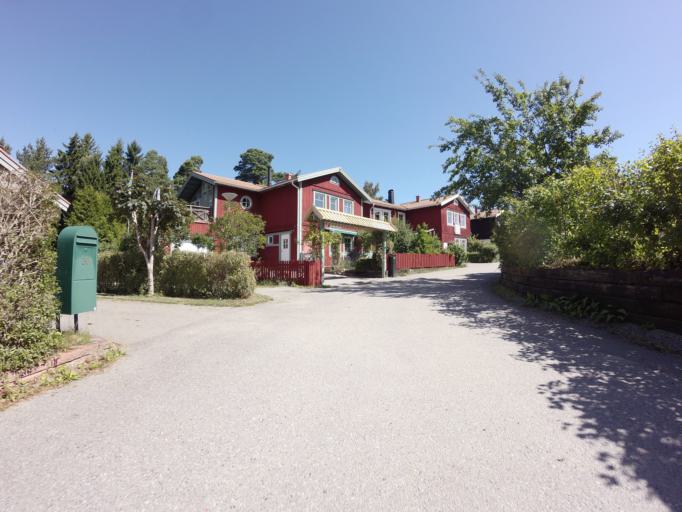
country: SE
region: Stockholm
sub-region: Jarfalla Kommun
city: Jakobsberg
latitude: 59.4622
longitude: 17.8823
